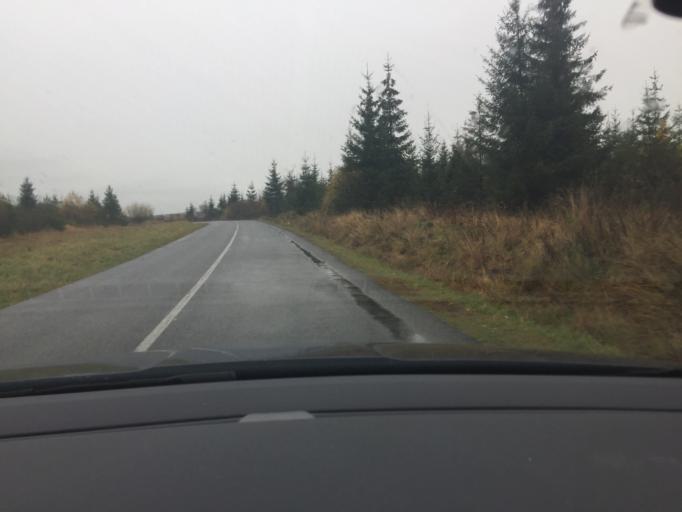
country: SK
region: Presovsky
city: Spisska Bela
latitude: 49.2046
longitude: 20.3734
